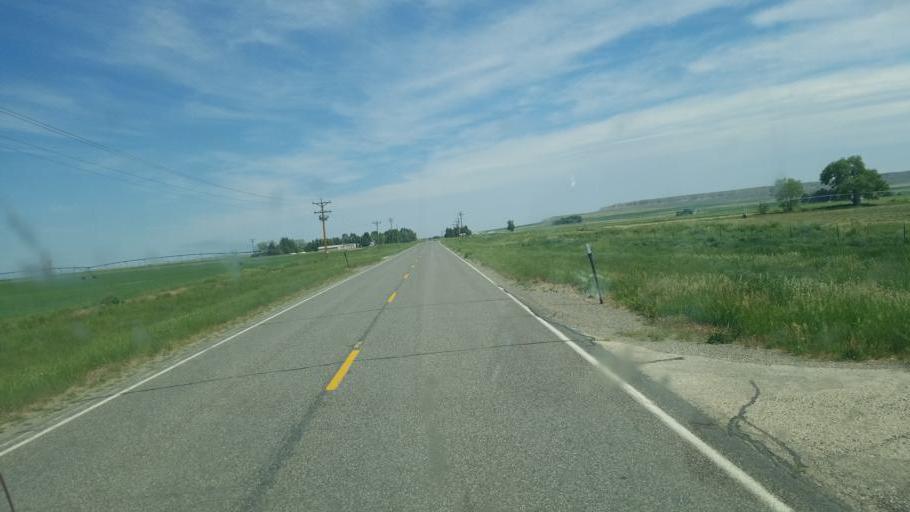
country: US
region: Wyoming
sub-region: Park County
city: Powell
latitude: 44.7459
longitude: -108.9327
